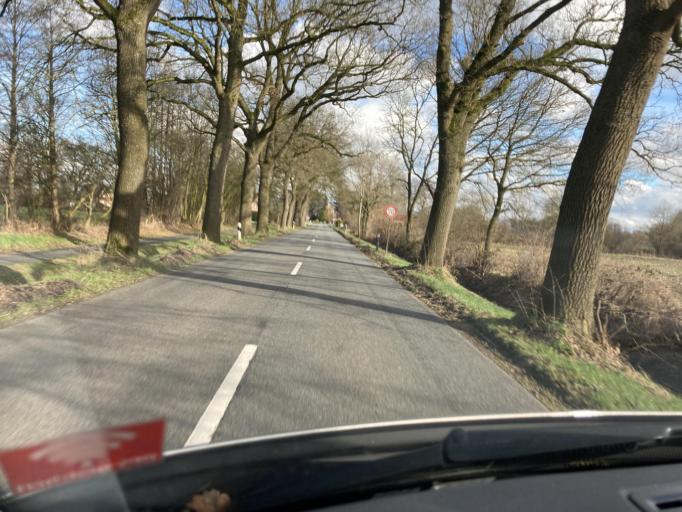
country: DE
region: Lower Saxony
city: Detern
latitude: 53.2492
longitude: 7.6769
